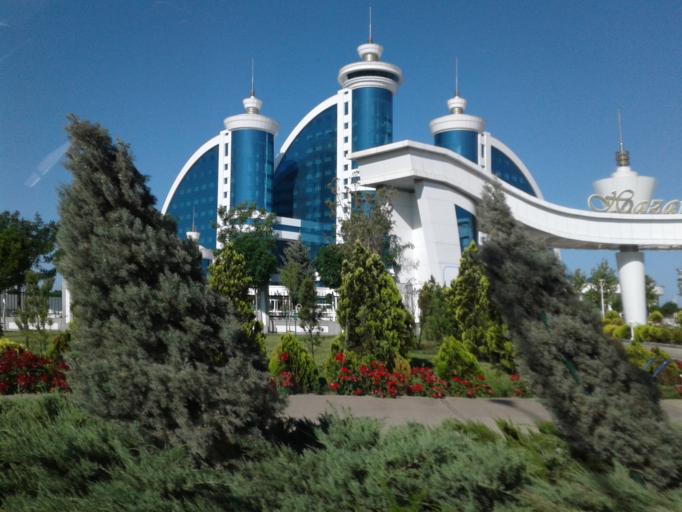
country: TM
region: Balkan
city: Turkmenbasy
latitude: 39.9812
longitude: 52.8266
